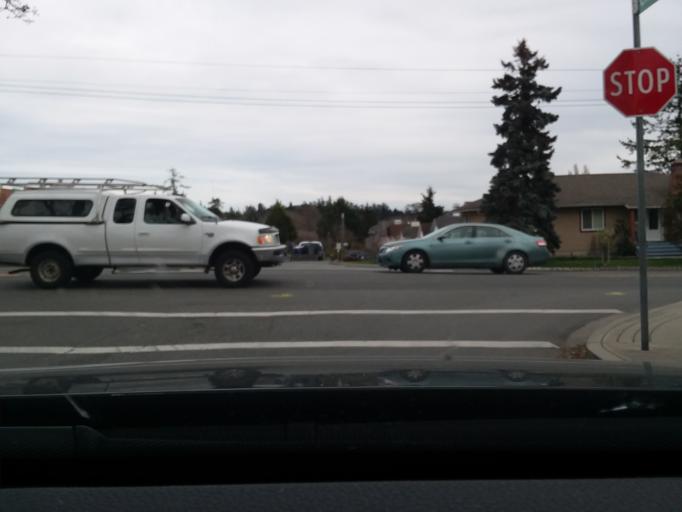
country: CA
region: British Columbia
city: Victoria
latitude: 48.4810
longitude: -123.4095
